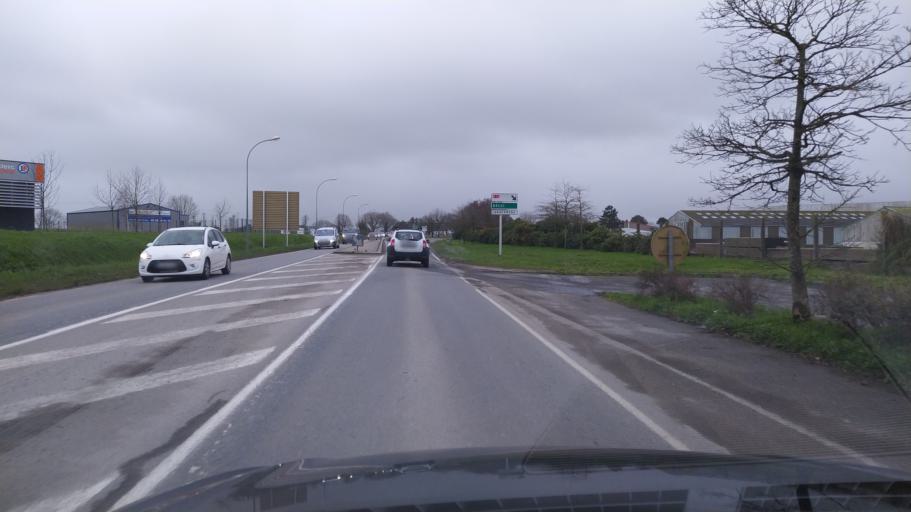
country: FR
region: Brittany
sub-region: Departement du Finistere
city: Landivisiau
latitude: 48.5216
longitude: -4.0594
